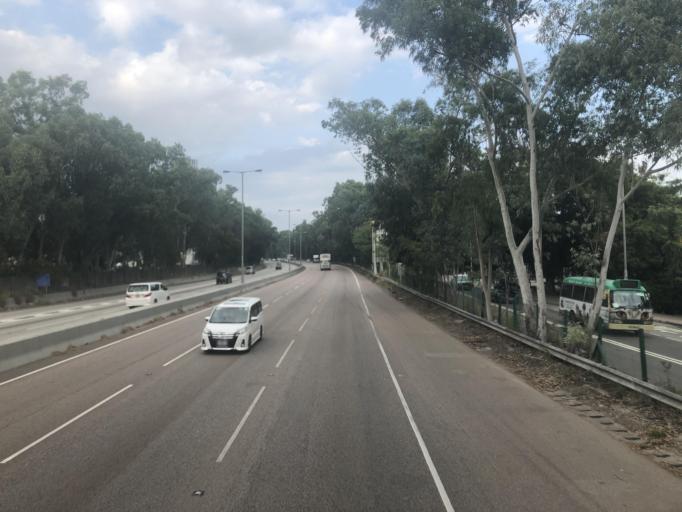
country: HK
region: Yuen Long
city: Yuen Long Kau Hui
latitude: 22.4757
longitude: 114.0570
